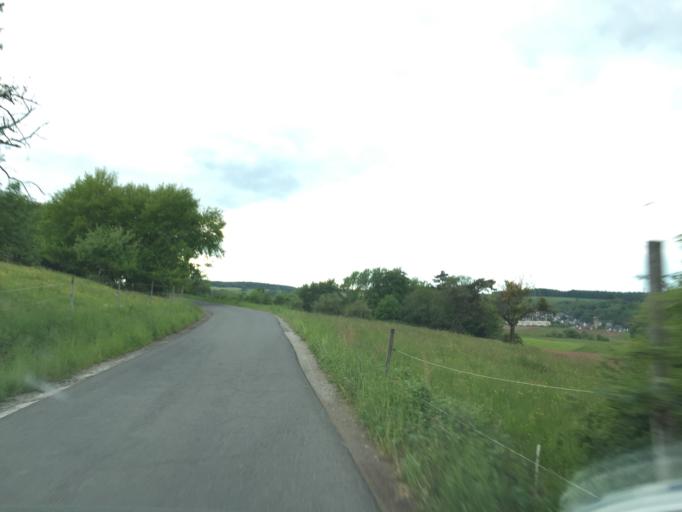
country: DE
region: Bavaria
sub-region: Regierungsbezirk Unterfranken
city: Waldaschaff
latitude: 49.9637
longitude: 9.2636
